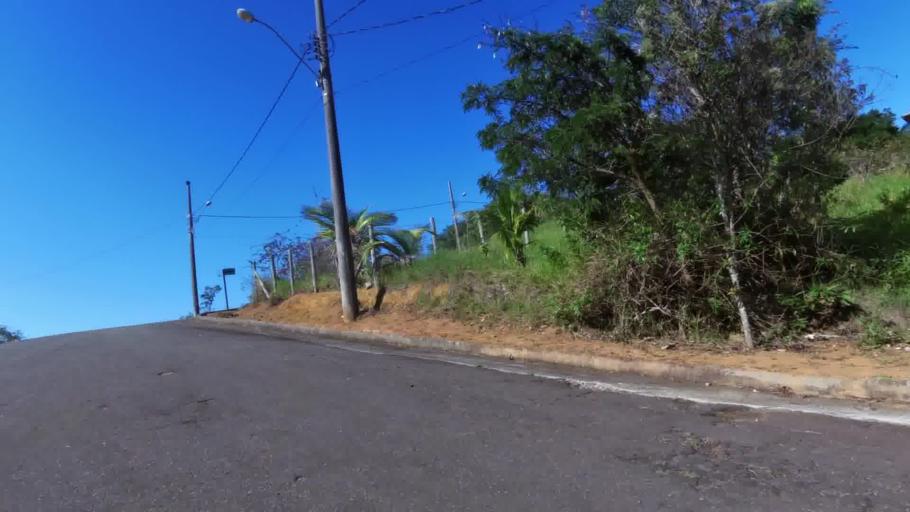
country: BR
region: Espirito Santo
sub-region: Guarapari
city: Guarapari
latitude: -20.7399
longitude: -40.5596
